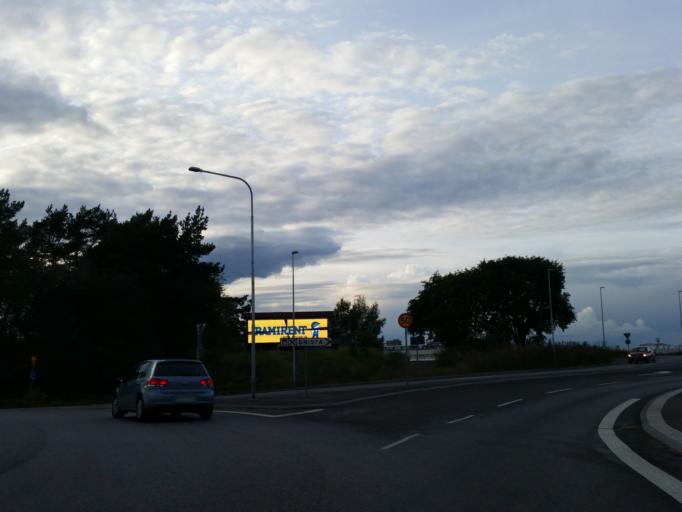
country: SE
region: Uppsala
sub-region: Uppsala Kommun
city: Saevja
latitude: 59.8431
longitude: 17.7110
